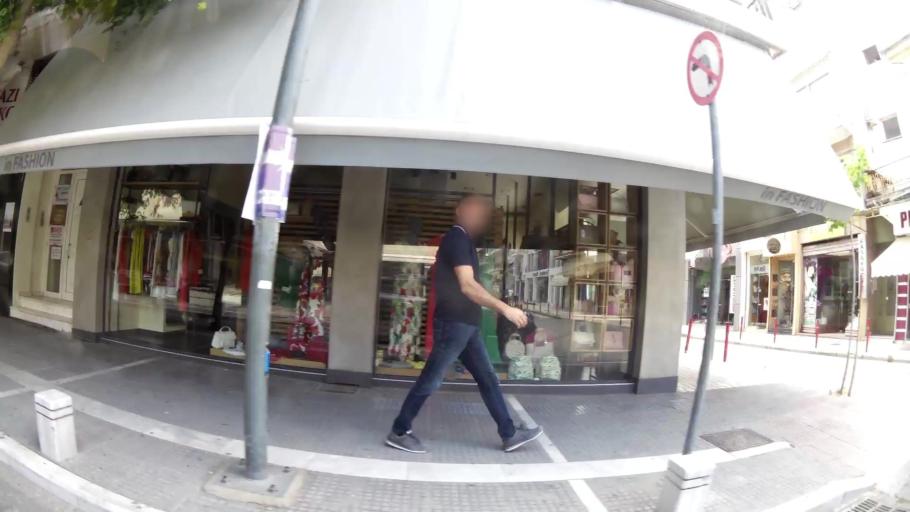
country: GR
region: Central Macedonia
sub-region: Nomos Pierias
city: Katerini
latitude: 40.2720
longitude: 22.5077
